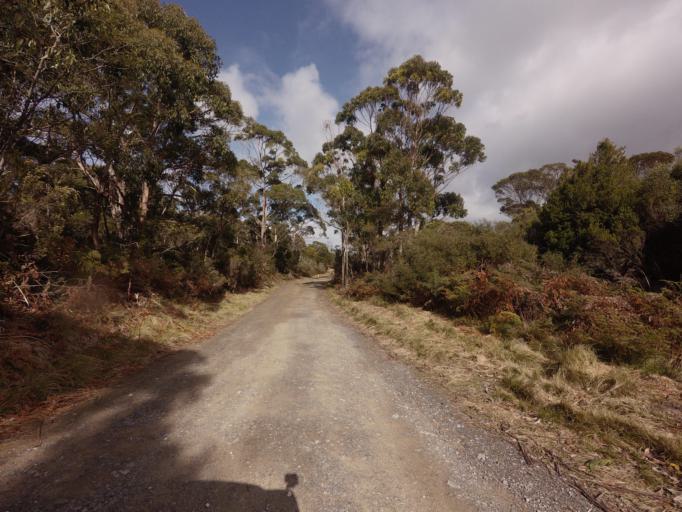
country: AU
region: Tasmania
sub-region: Huon Valley
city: Geeveston
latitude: -43.5792
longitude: 146.9005
